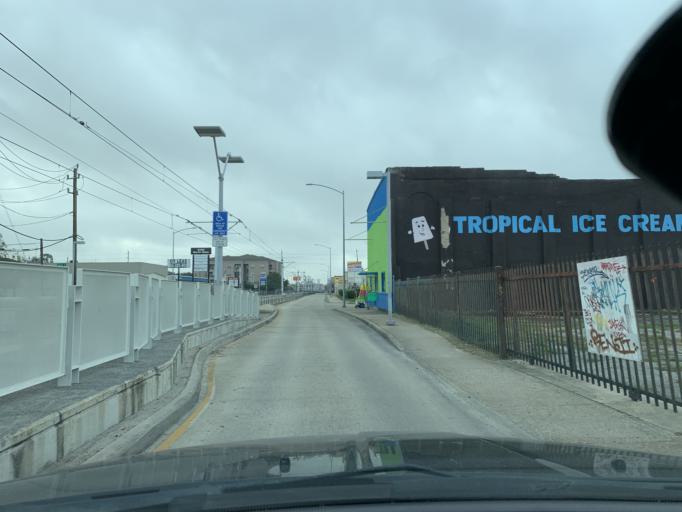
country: US
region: Texas
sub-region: Harris County
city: Houston
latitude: 29.7801
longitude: -95.3636
